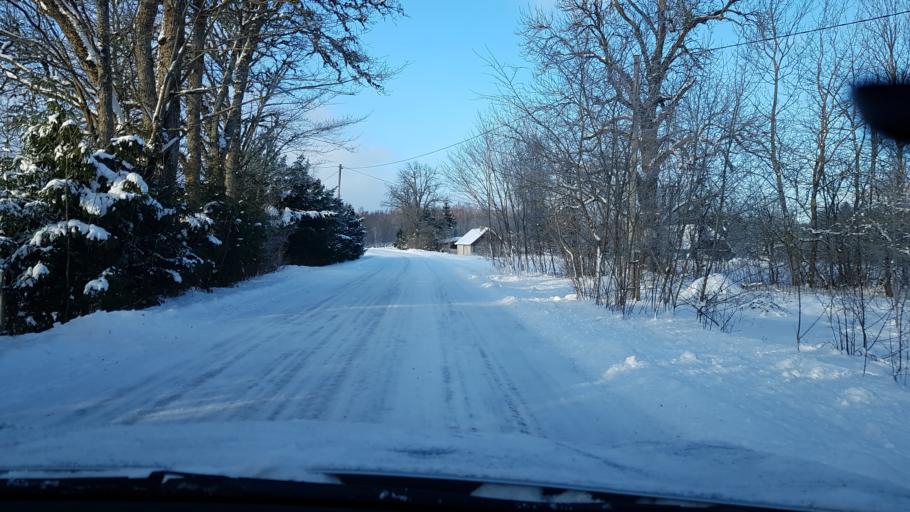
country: EE
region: Harju
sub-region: Nissi vald
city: Turba
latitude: 59.1055
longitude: 24.2354
